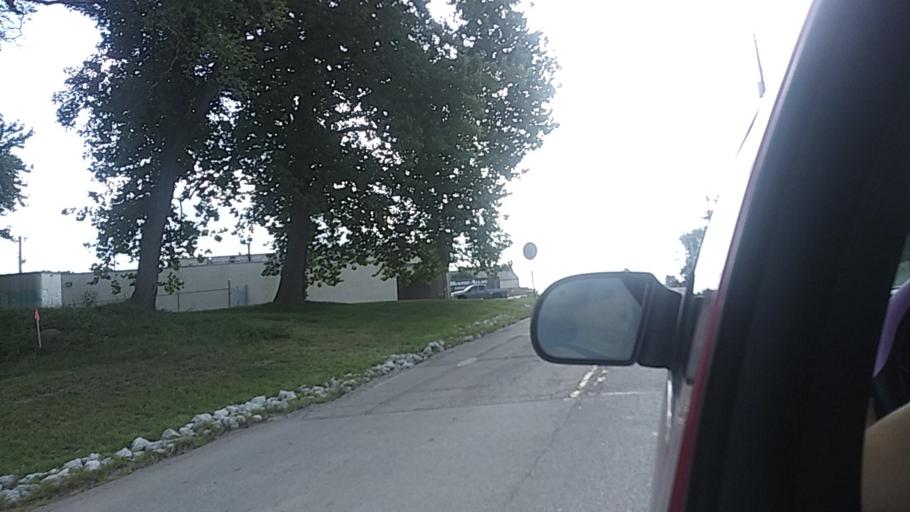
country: US
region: Ohio
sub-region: Summit County
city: Akron
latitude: 41.0949
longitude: -81.4831
